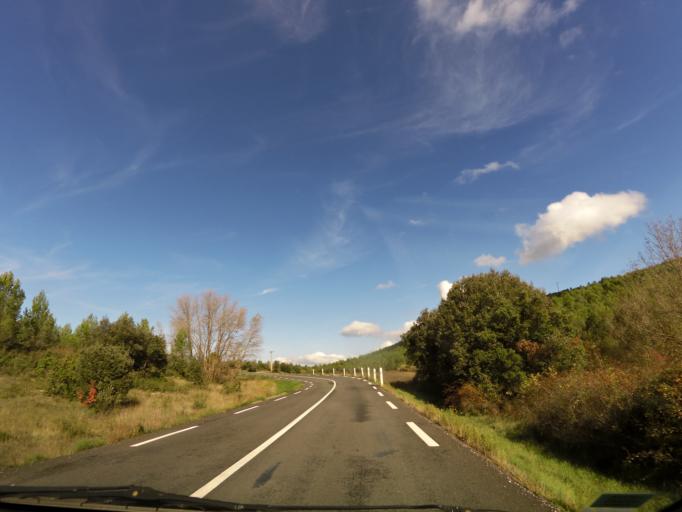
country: FR
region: Languedoc-Roussillon
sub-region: Departement du Gard
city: Villevieille
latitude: 43.8542
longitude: 4.0967
